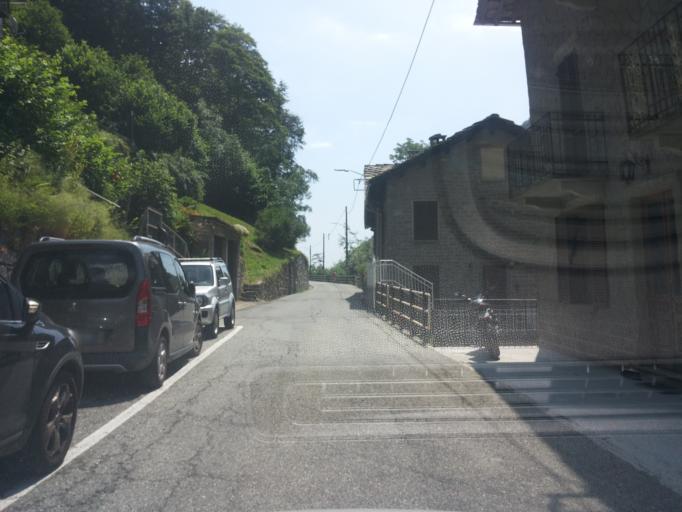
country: IT
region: Piedmont
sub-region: Provincia di Biella
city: Piedicavallo
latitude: 45.6871
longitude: 7.9594
